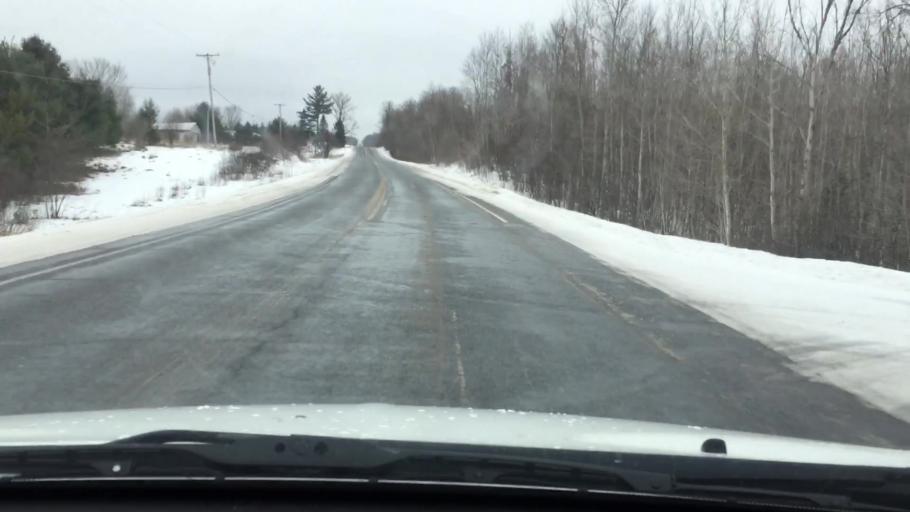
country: US
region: Michigan
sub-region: Wexford County
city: Cadillac
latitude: 44.1132
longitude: -85.4442
